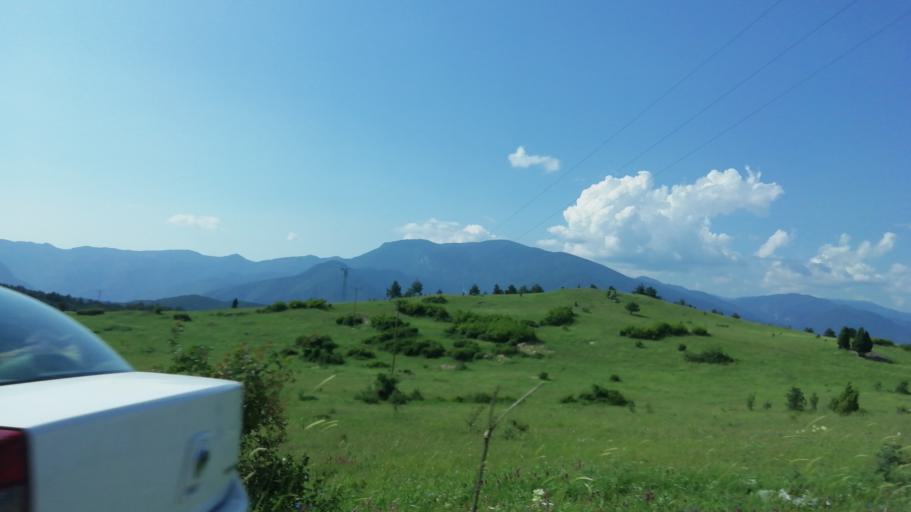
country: TR
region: Karabuk
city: Karabuk
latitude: 41.1305
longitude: 32.5745
